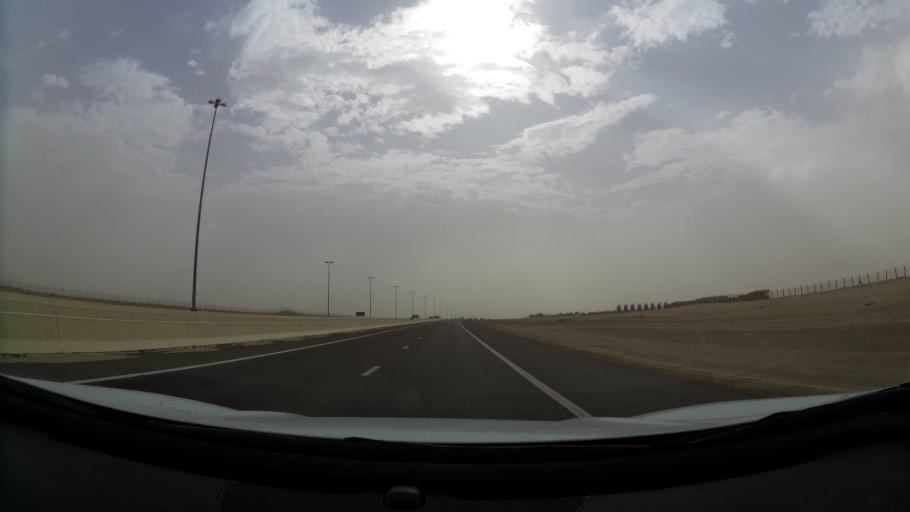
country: AE
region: Abu Dhabi
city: Abu Dhabi
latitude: 24.4787
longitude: 54.6627
